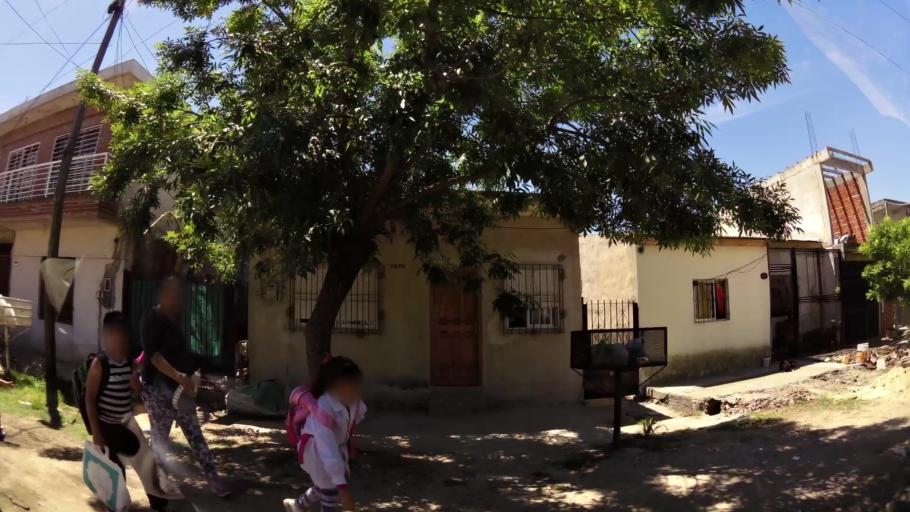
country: AR
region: Buenos Aires
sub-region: Partido de Quilmes
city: Quilmes
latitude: -34.7140
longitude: -58.3185
